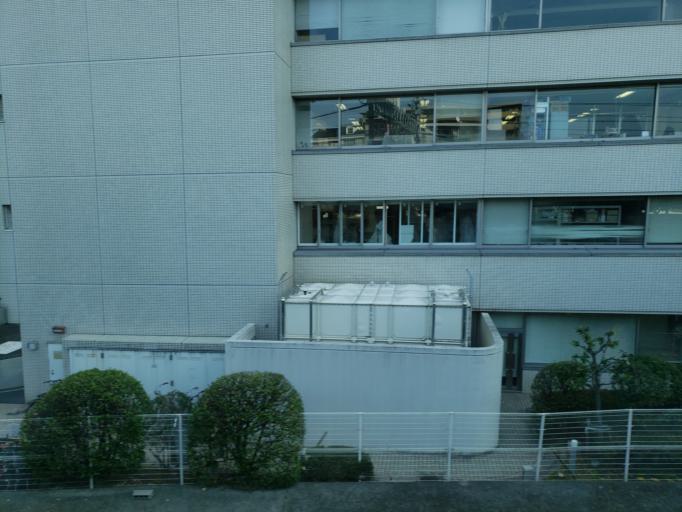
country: JP
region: Hyogo
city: Nishinomiya-hama
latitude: 34.7389
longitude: 135.3421
